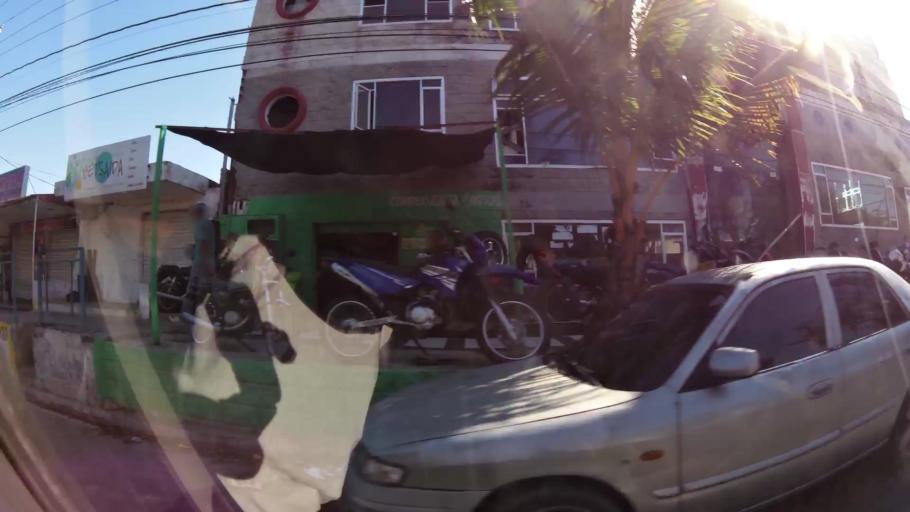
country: CO
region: Atlantico
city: Barranquilla
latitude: 10.9461
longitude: -74.7964
